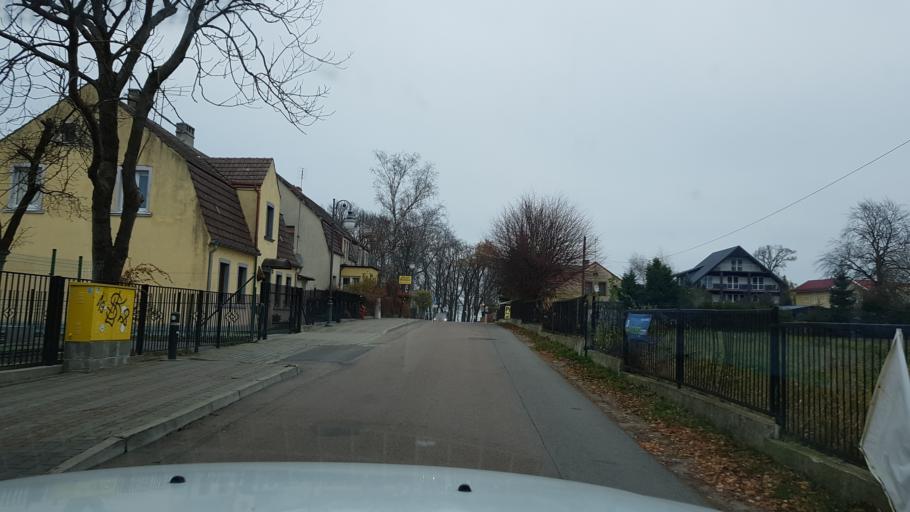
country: PL
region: West Pomeranian Voivodeship
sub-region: Powiat gryficki
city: Rewal
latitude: 54.0822
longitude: 15.0165
